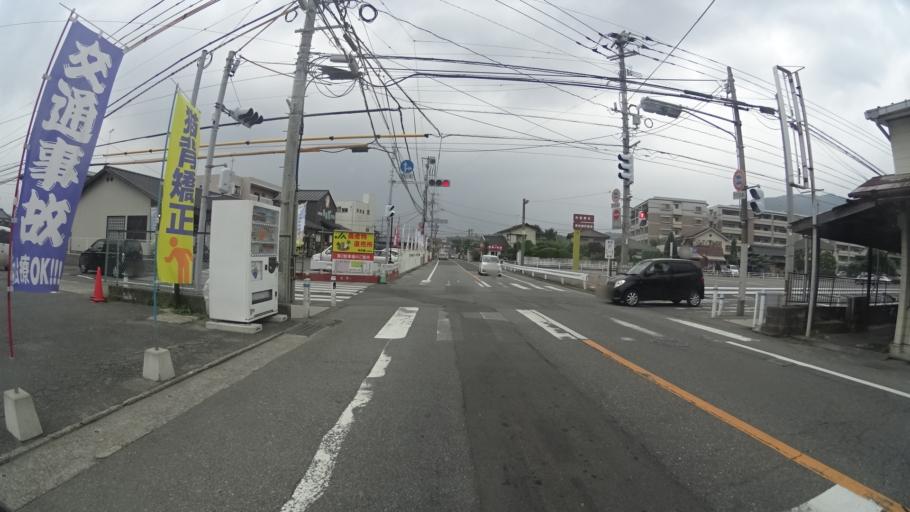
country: JP
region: Fukuoka
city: Dazaifu
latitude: 33.5165
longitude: 130.5320
